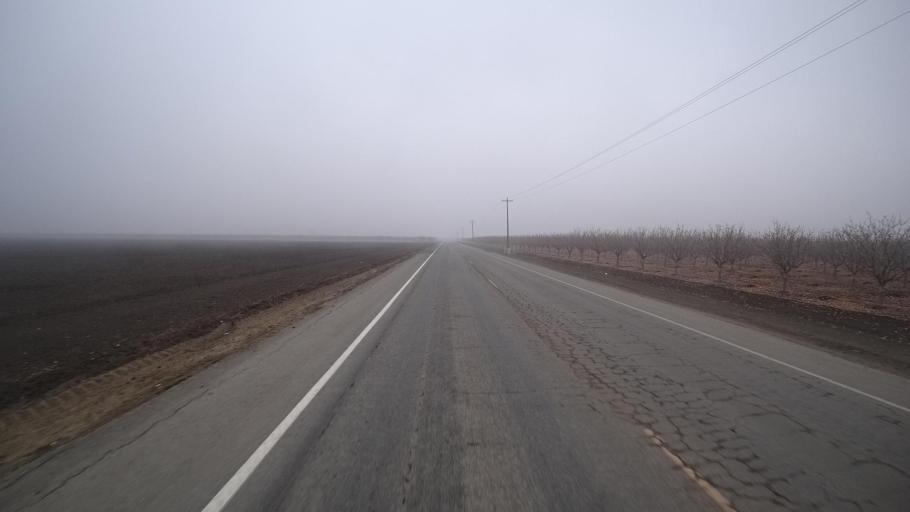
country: US
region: California
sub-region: Kern County
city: Buttonwillow
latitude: 35.4053
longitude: -119.5184
